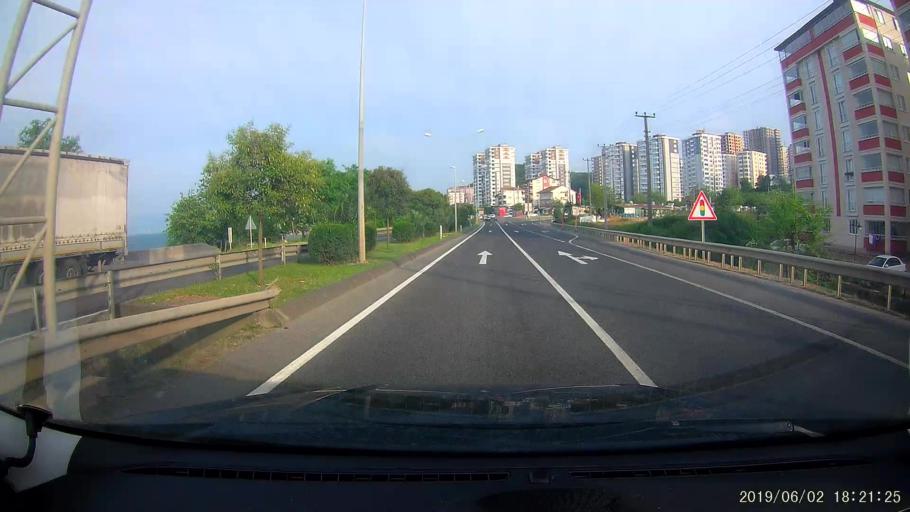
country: TR
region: Ordu
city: Fatsa
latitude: 41.0653
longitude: 37.4687
